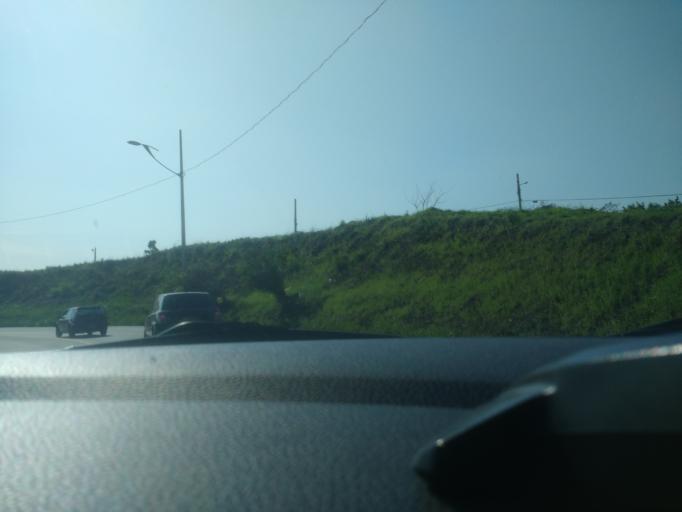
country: BR
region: Rio de Janeiro
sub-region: Duque De Caxias
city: Duque de Caxias
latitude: -22.8002
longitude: -43.2897
